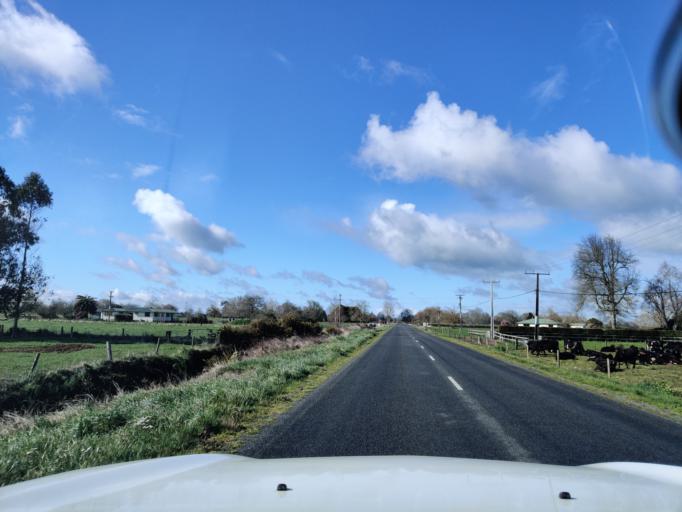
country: NZ
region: Waikato
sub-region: Waikato District
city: Ngaruawahia
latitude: -37.6064
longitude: 175.3057
